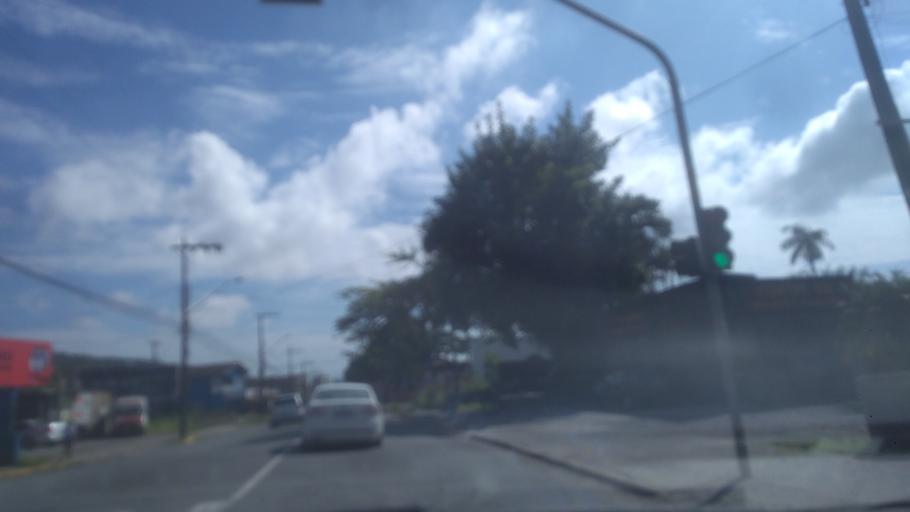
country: BR
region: Santa Catarina
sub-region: Joinville
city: Joinville
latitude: -26.3079
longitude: -48.8271
